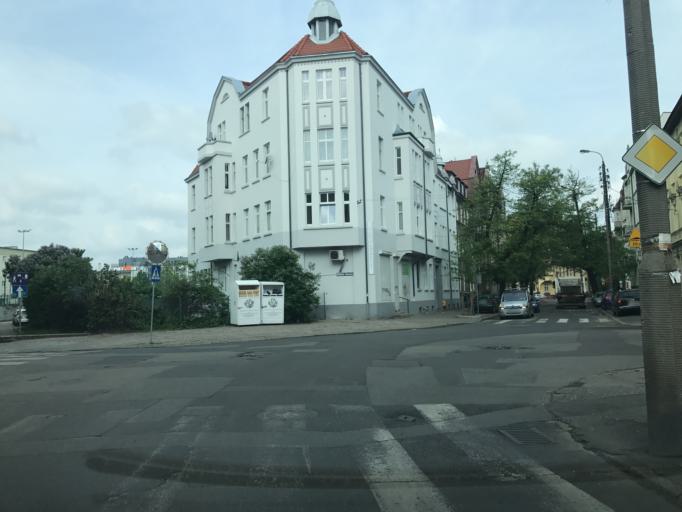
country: PL
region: Kujawsko-Pomorskie
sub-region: Bydgoszcz
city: Bydgoszcz
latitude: 53.1282
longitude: 17.9893
